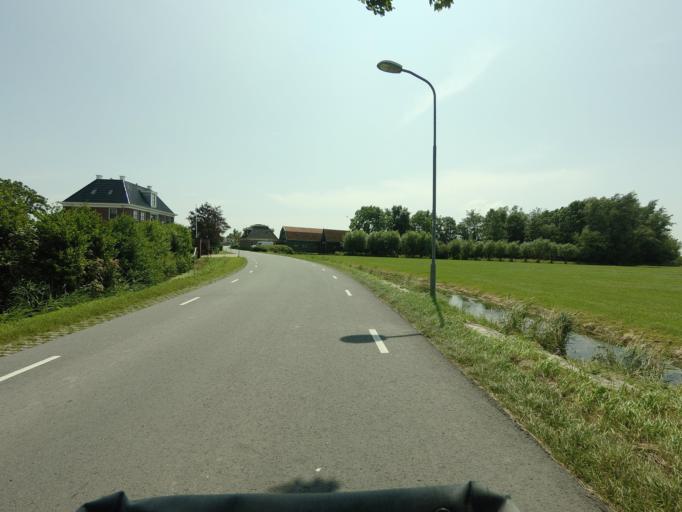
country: NL
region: North Holland
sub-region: Gemeente Opmeer
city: Opmeer
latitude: 52.6604
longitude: 4.9480
